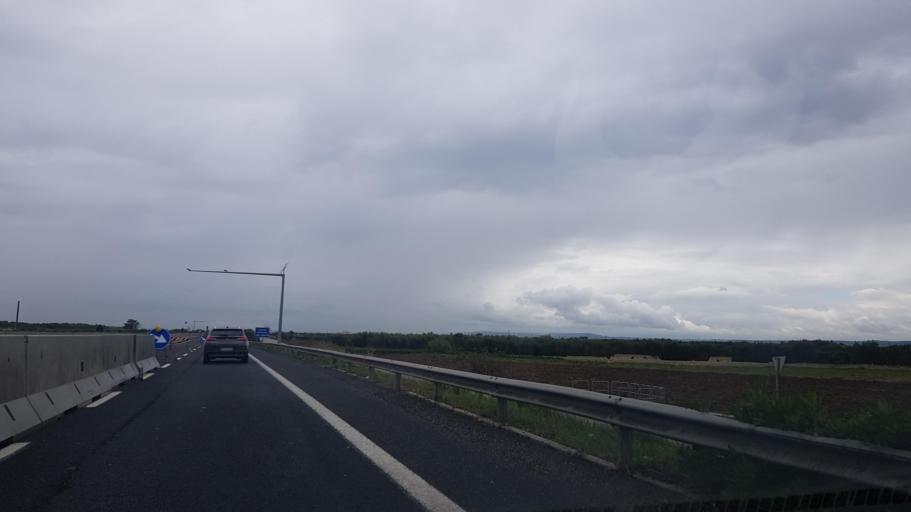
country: IT
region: Apulia
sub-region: Provincia di Taranto
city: Massafra
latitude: 40.5313
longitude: 17.1089
